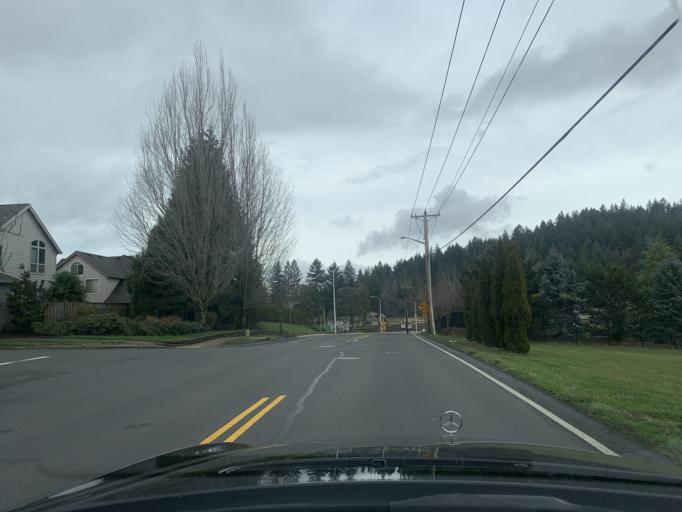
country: US
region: Oregon
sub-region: Clackamas County
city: Happy Valley
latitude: 45.4397
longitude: -122.5122
